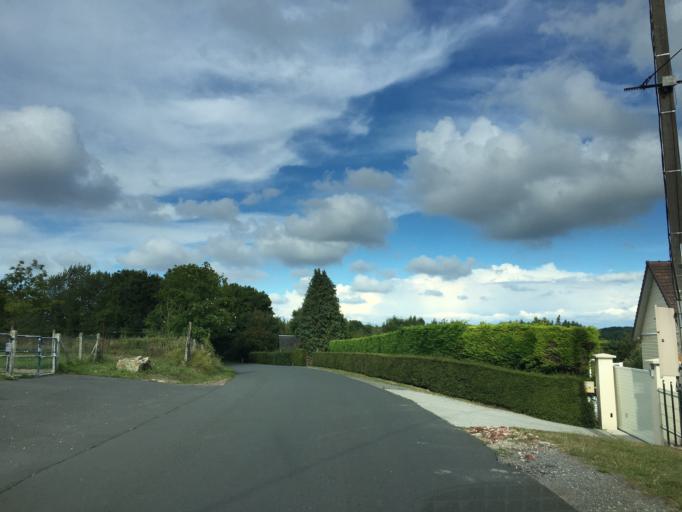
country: FR
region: Lower Normandy
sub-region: Departement du Calvados
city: Houlgate
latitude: 49.3015
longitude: -0.0586
